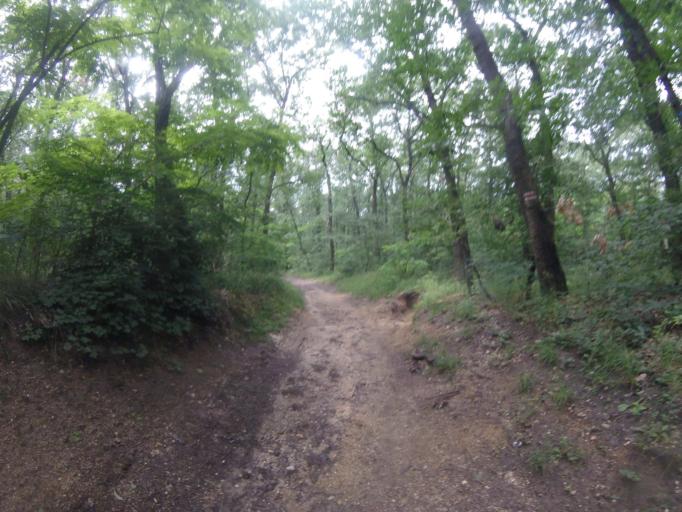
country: HU
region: Pest
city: Toeroekbalint
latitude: 47.4241
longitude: 18.9169
